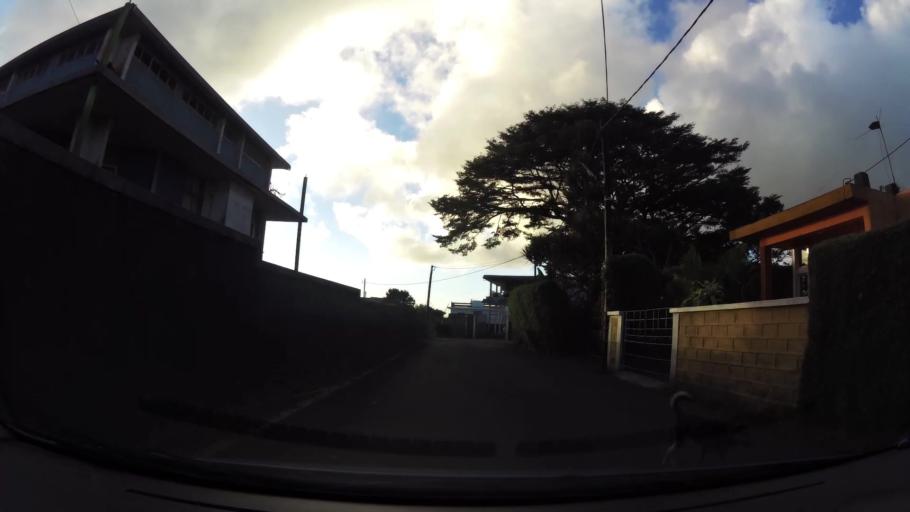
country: MU
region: Plaines Wilhems
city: Curepipe
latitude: -20.3085
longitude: 57.5303
